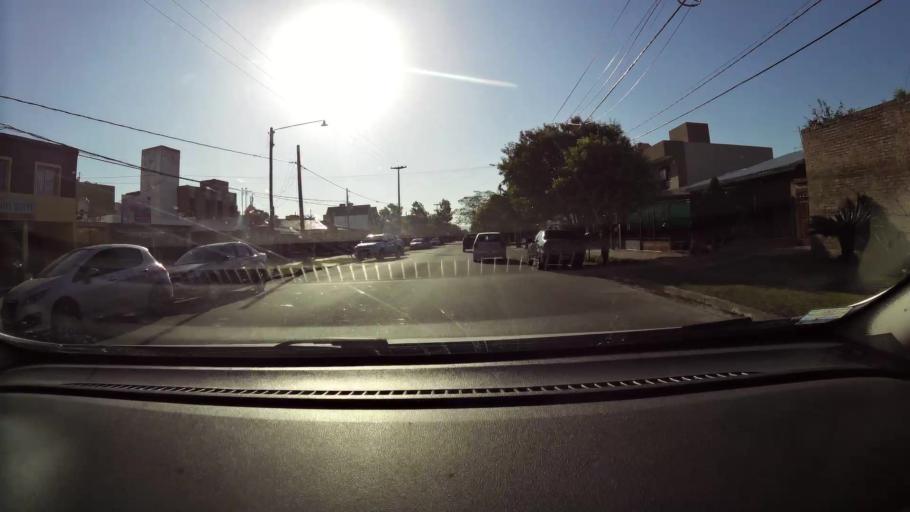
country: AR
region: Cordoba
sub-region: Departamento de Capital
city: Cordoba
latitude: -31.3608
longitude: -64.2137
